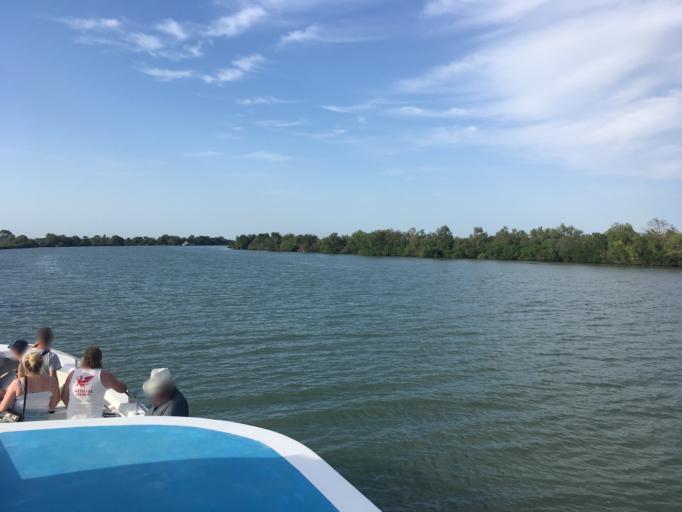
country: FR
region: Provence-Alpes-Cote d'Azur
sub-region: Departement des Bouches-du-Rhone
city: Saintes-Maries-de-la-Mer
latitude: 43.4763
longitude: 4.3767
